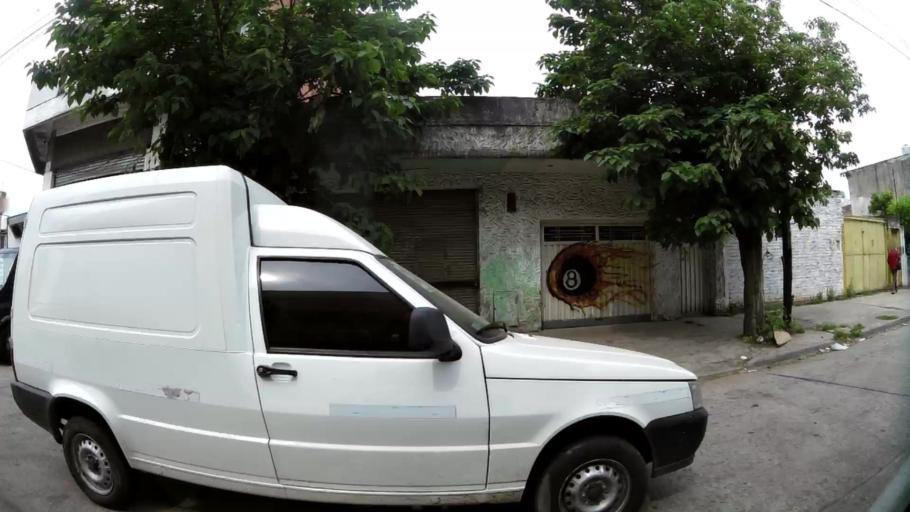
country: AR
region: Buenos Aires
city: San Justo
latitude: -34.6986
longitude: -58.5277
